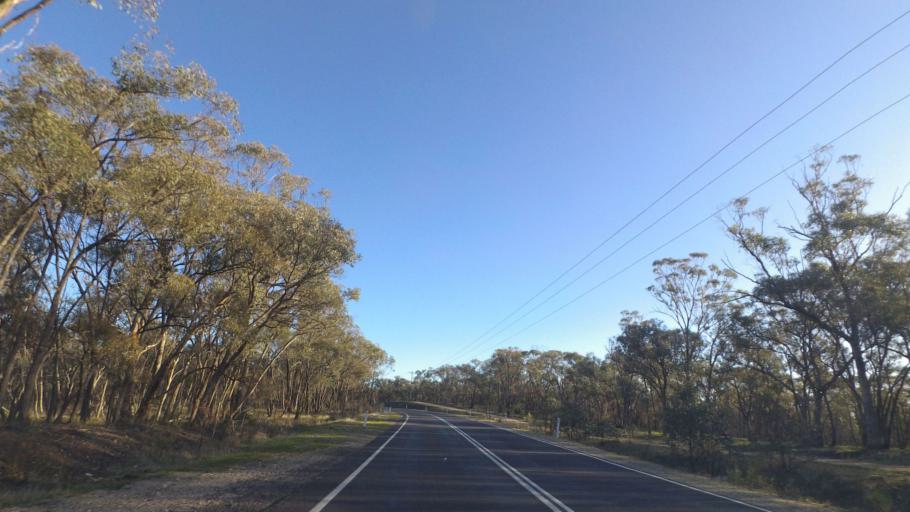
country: AU
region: Victoria
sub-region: Greater Bendigo
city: Kennington
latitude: -36.8754
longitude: 144.4945
